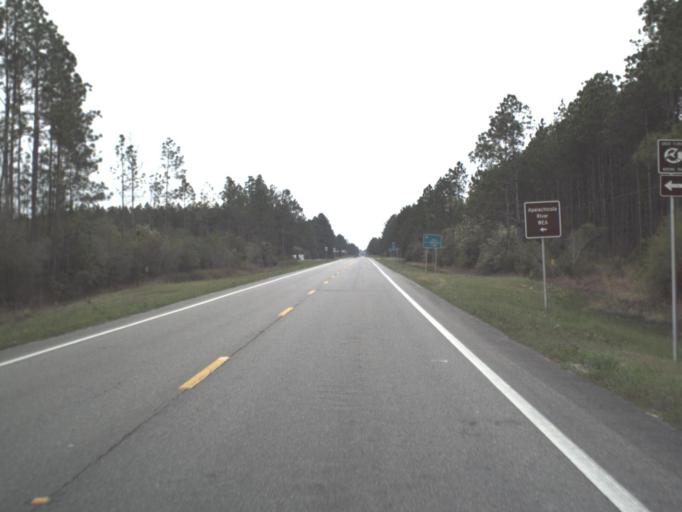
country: US
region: Florida
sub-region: Gulf County
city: Port Saint Joe
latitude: 29.9126
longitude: -85.2038
